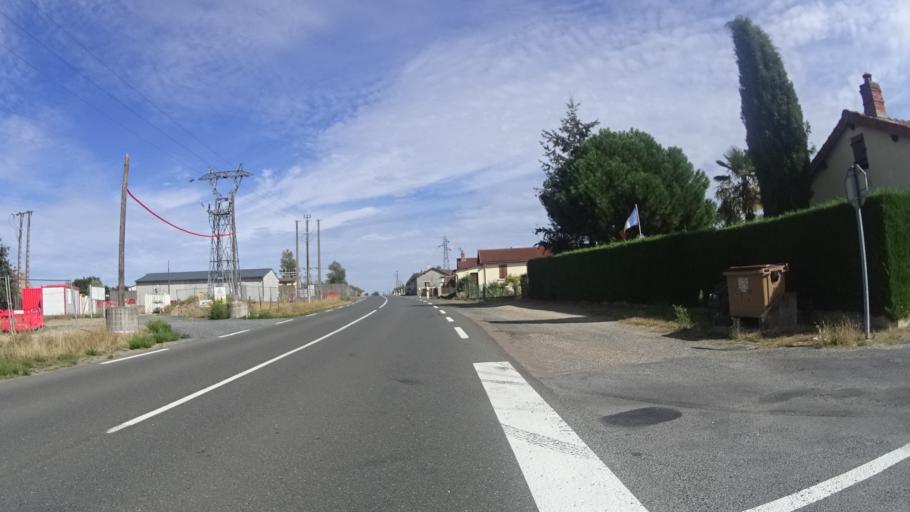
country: FR
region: Bourgogne
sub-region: Departement de Saone-et-Loire
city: Bourbon-Lancy
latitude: 46.6210
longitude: 3.7394
